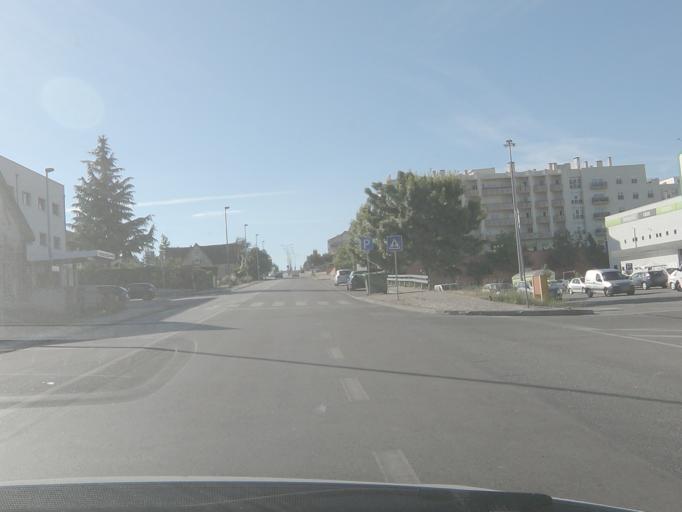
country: PT
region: Viseu
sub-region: Viseu
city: Abraveses
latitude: 40.6730
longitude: -7.9208
